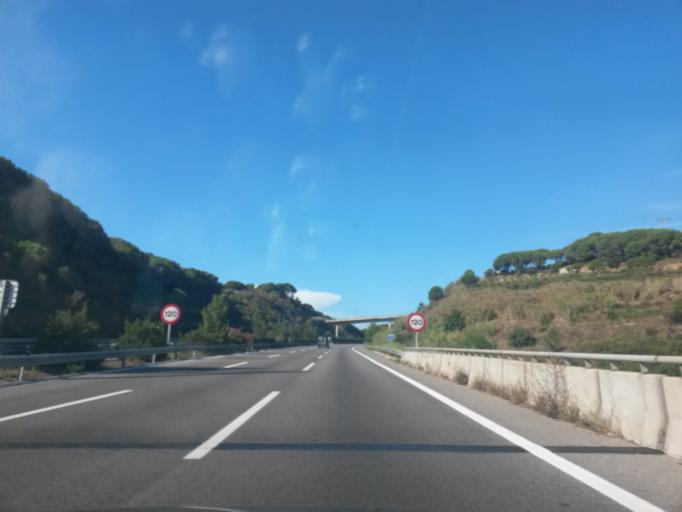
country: ES
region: Catalonia
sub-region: Provincia de Barcelona
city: Sant Pol de Mar
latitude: 41.6042
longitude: 2.6047
